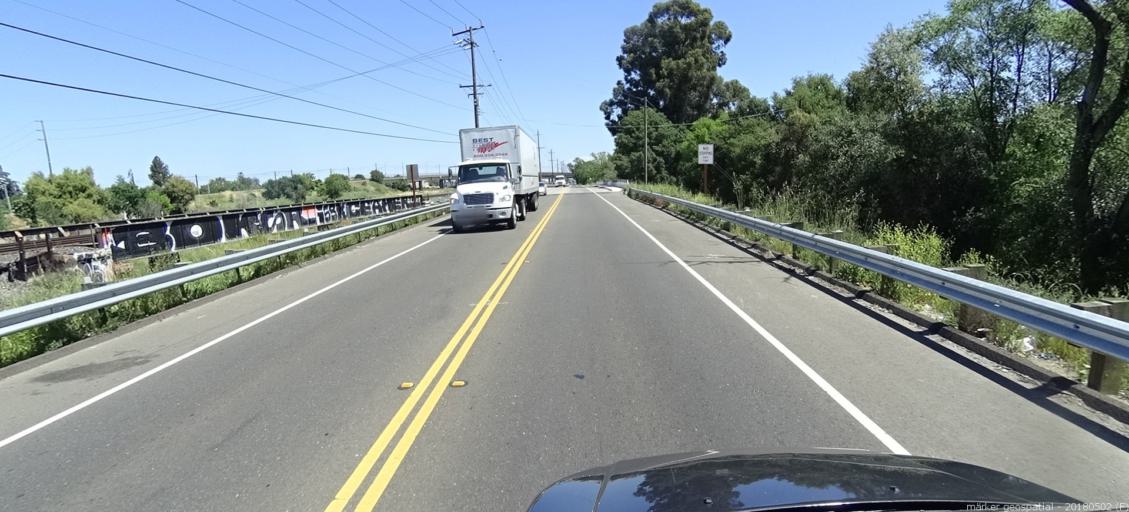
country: US
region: California
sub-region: Sacramento County
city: Arden-Arcade
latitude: 38.6306
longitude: -121.4137
